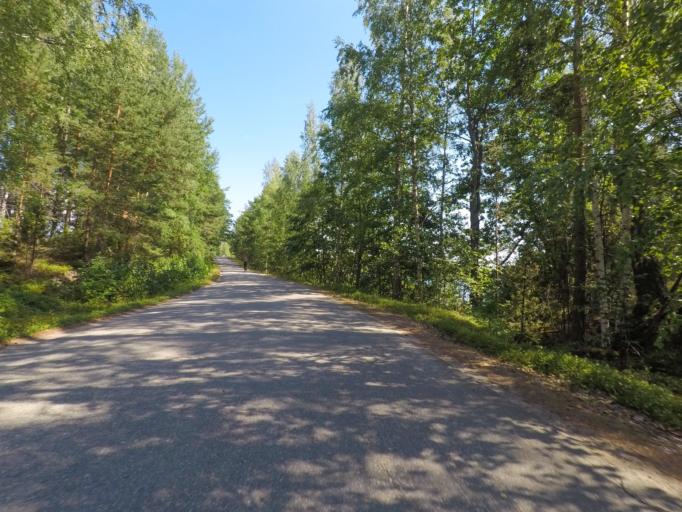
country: FI
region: Southern Savonia
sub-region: Mikkeli
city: Puumala
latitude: 61.4054
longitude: 28.0678
